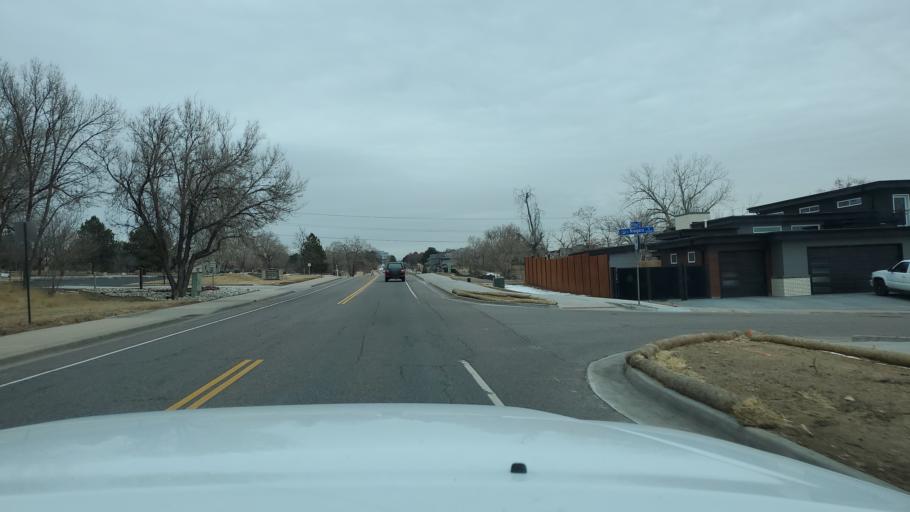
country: US
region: Colorado
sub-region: Arapahoe County
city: Castlewood
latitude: 39.6095
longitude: -104.9116
